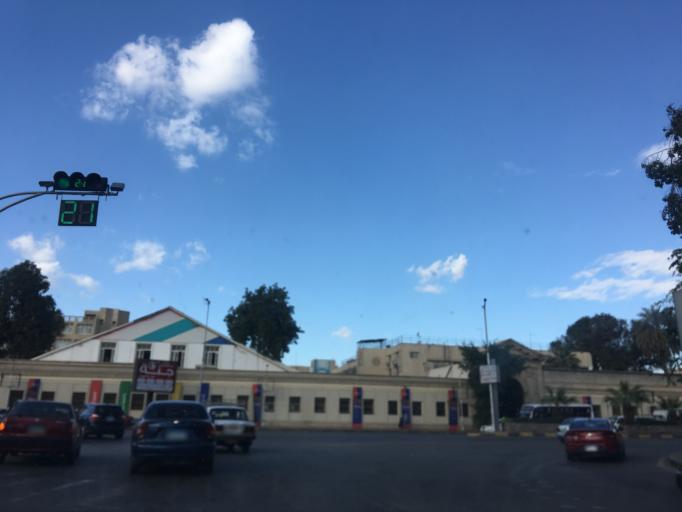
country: EG
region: Al Jizah
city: Al Jizah
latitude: 30.0294
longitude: 31.2103
